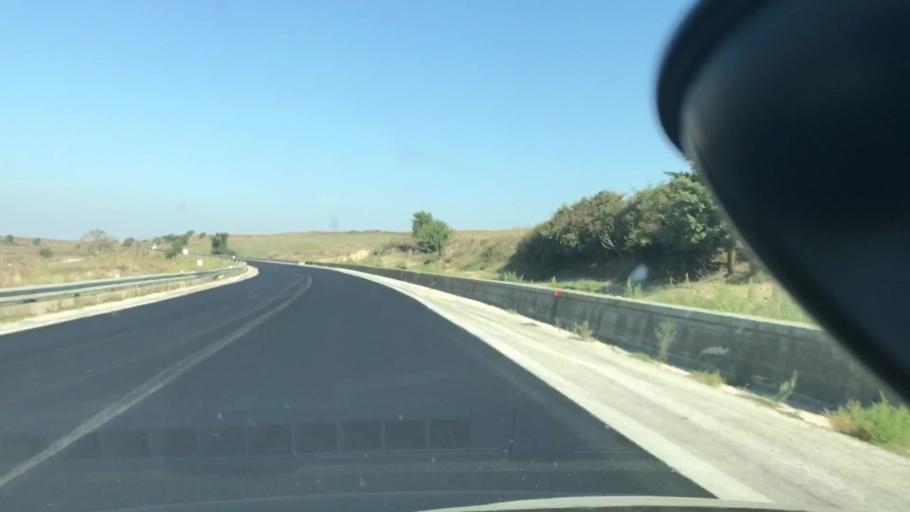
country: IT
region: Apulia
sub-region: Provincia di Barletta - Andria - Trani
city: Spinazzola
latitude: 40.9010
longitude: 16.1204
